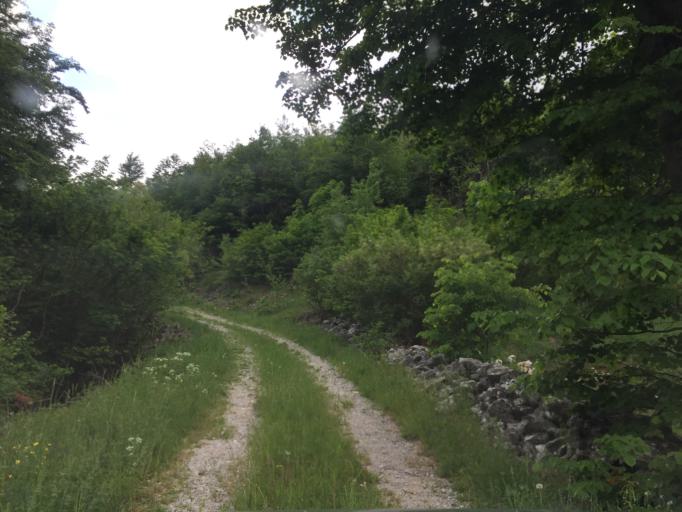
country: SI
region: Nova Gorica
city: Sempas
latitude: 46.0380
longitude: 13.7687
